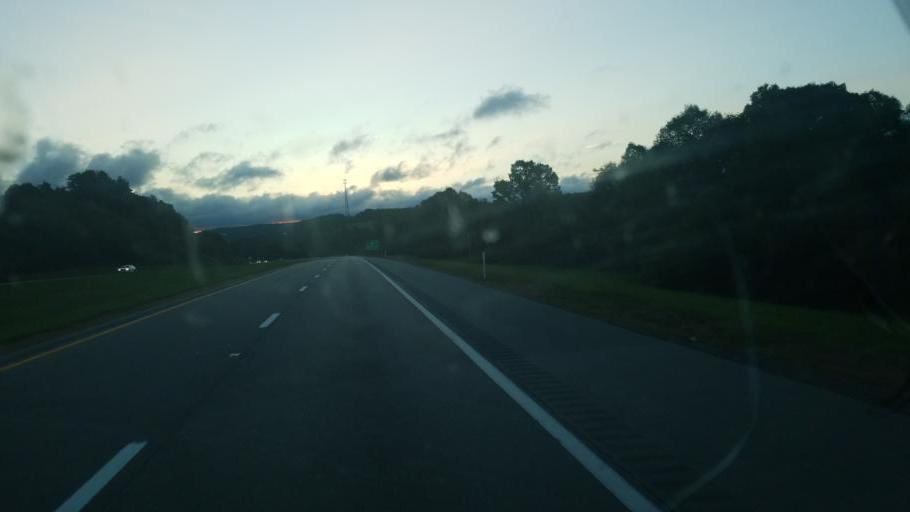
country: US
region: West Virginia
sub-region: Preston County
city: Terra Alta
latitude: 39.6566
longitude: -79.5499
